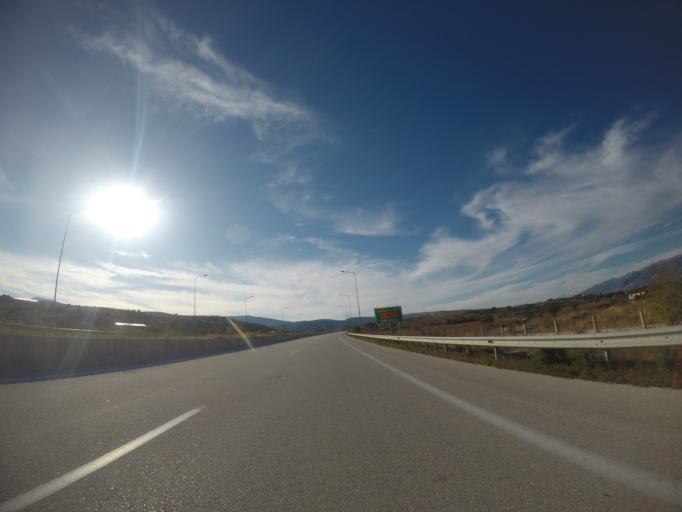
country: GR
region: Epirus
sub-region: Nomos Ioanninon
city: Koutselio
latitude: 39.6009
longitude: 20.8998
